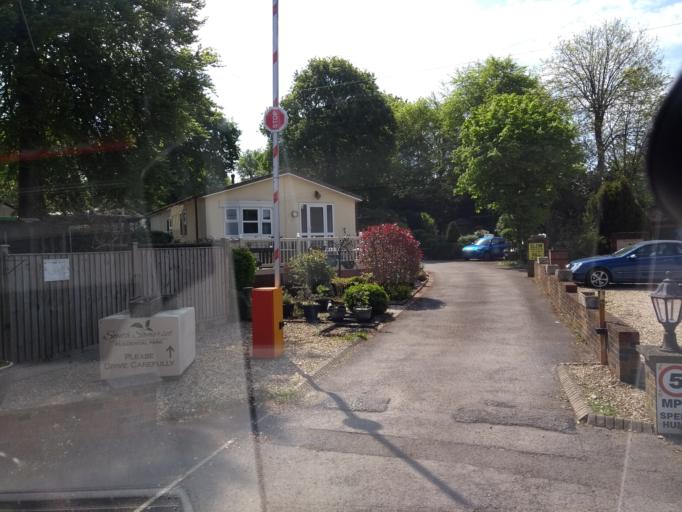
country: GB
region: England
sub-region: Somerset
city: Chard
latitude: 50.8805
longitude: -3.0283
